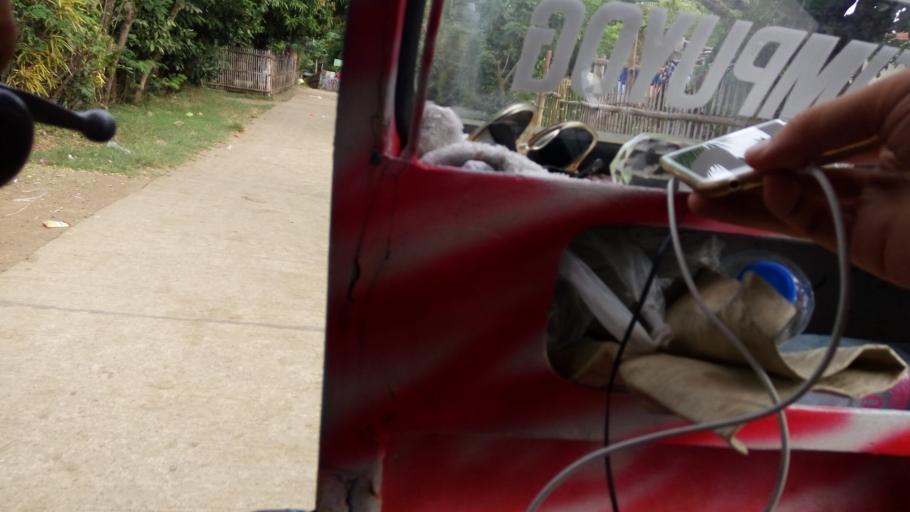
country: PH
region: Ilocos
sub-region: Province of La Union
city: Payocpoc Sur
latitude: 16.5054
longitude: 120.3328
